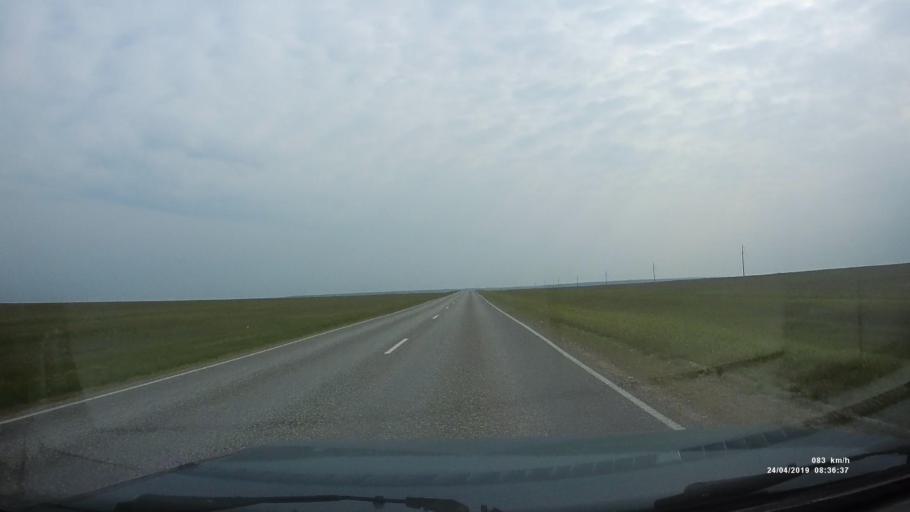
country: RU
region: Kalmykiya
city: Arshan'
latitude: 46.2057
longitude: 43.9376
